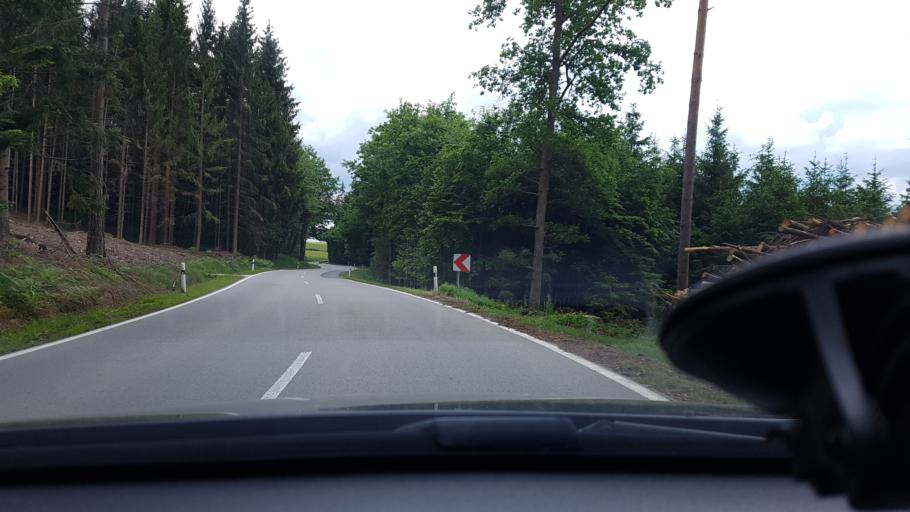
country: DE
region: Bavaria
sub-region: Lower Bavaria
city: Triftern
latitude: 48.3718
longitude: 13.0084
